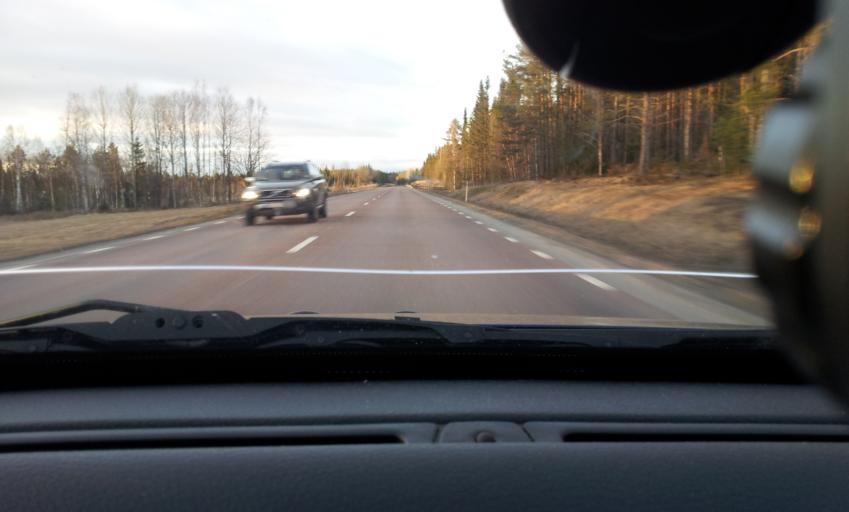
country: SE
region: Jaemtland
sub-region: Bergs Kommun
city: Hoverberg
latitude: 62.9317
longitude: 14.5384
